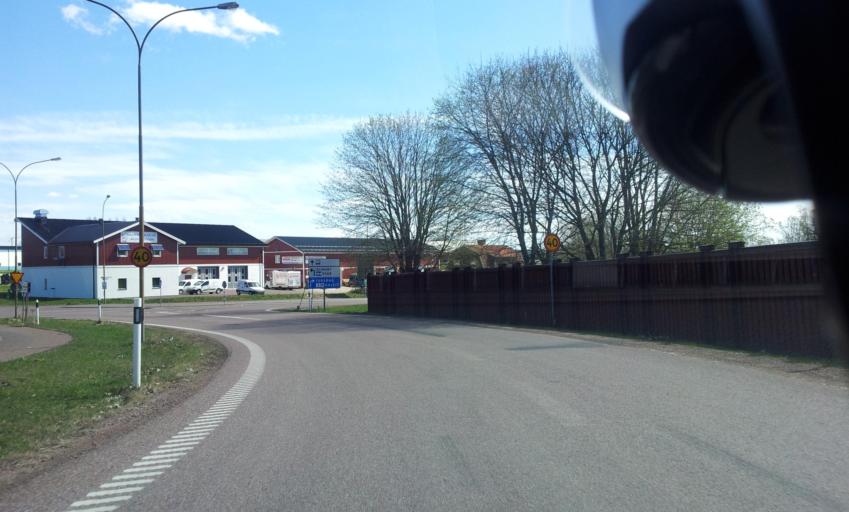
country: SE
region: Dalarna
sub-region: Borlange Kommun
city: Borlaenge
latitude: 60.4847
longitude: 15.4629
